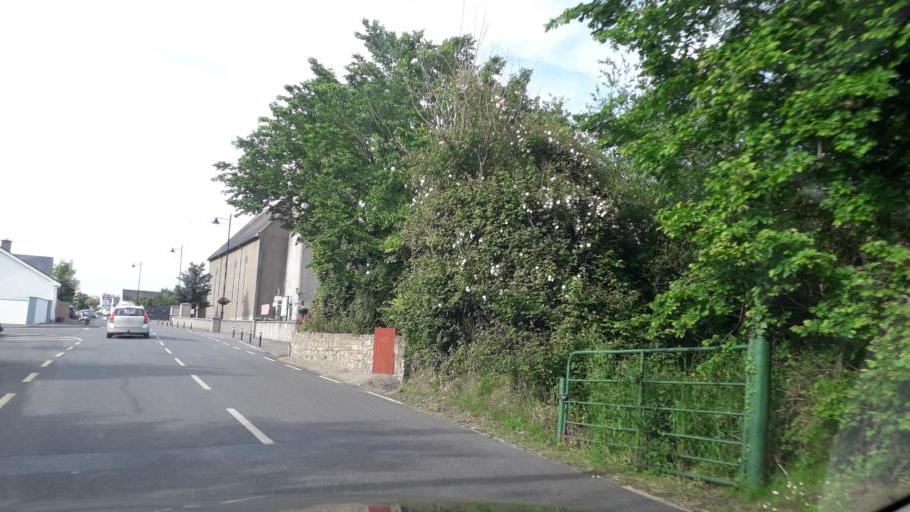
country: IE
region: Leinster
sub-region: Loch Garman
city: Courtown
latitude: 52.5723
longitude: -6.2303
